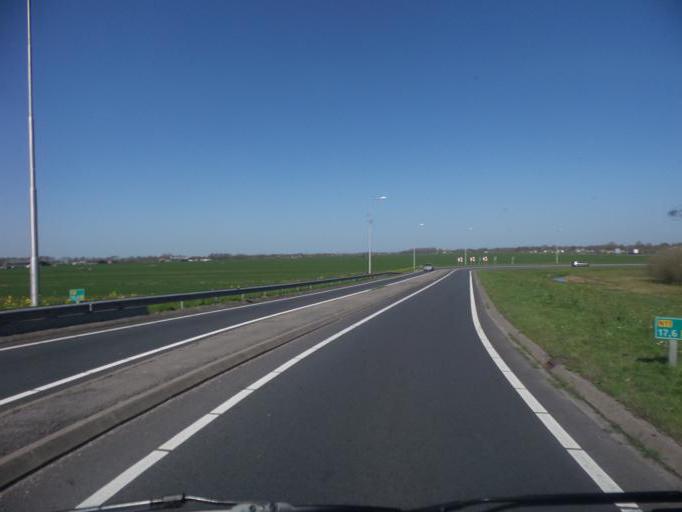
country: NL
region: South Holland
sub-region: Bodegraven-Reeuwijk
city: Bodegraven
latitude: 52.0873
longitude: 4.7324
